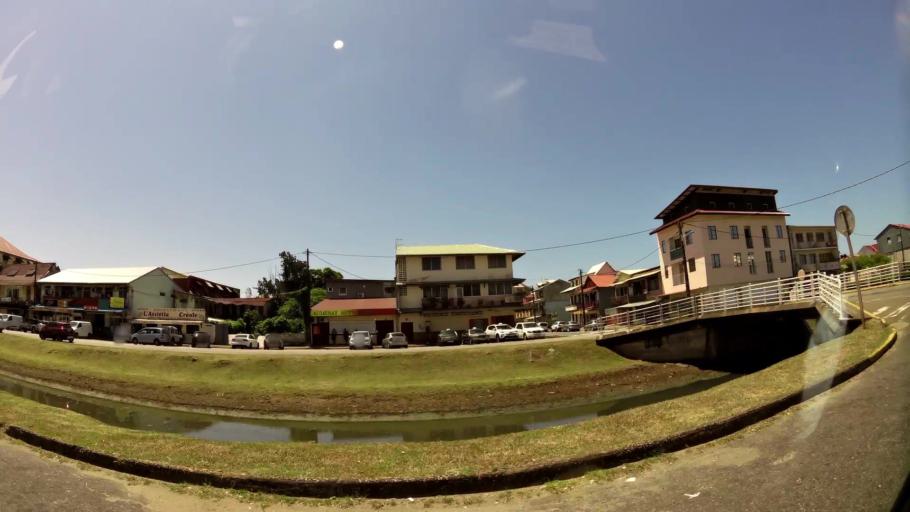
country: GF
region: Guyane
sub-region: Guyane
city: Cayenne
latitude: 4.9356
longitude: -52.3312
